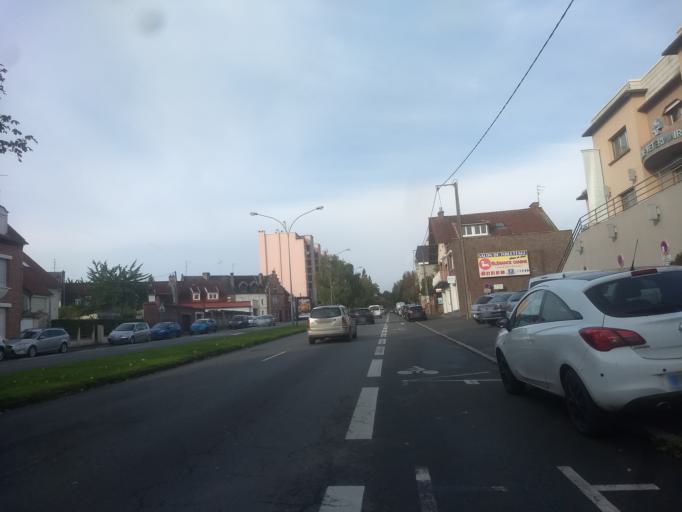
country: FR
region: Nord-Pas-de-Calais
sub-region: Departement du Pas-de-Calais
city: Sainte-Catherine
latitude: 50.2971
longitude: 2.7672
